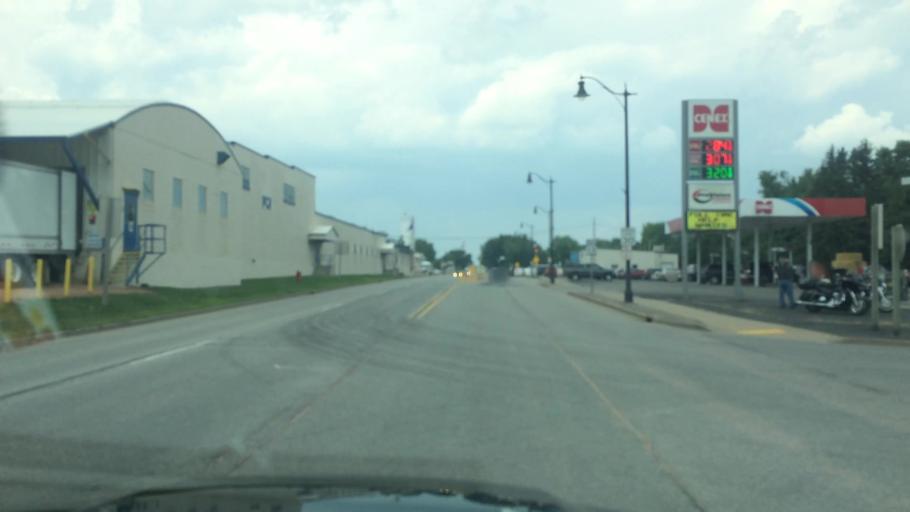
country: US
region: Wisconsin
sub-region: Clark County
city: Colby
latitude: 44.9023
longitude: -90.3151
